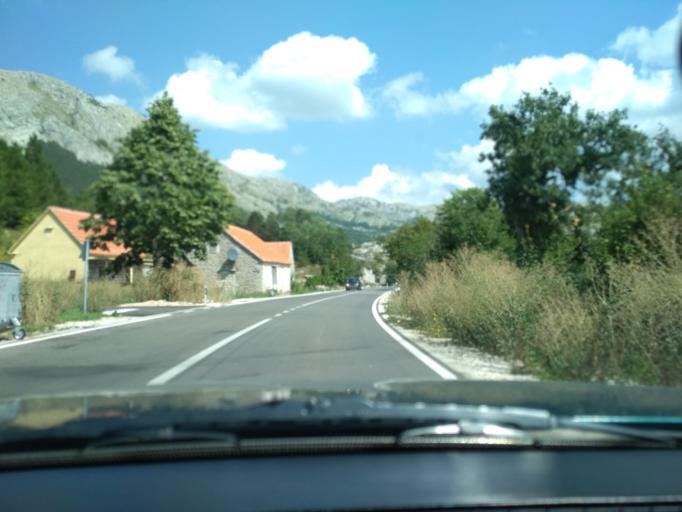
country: ME
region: Kotor
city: Kotor
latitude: 42.4309
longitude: 18.8071
